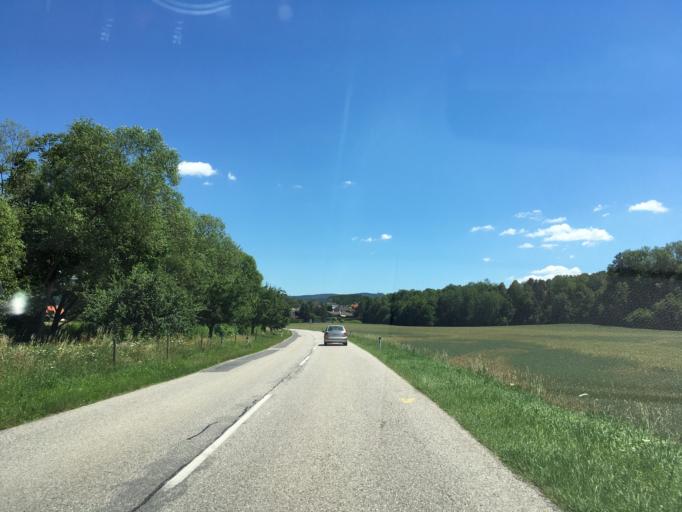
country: AT
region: Lower Austria
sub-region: Politischer Bezirk Wiener Neustadt
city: Bad Erlach
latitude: 47.7211
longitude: 16.2031
